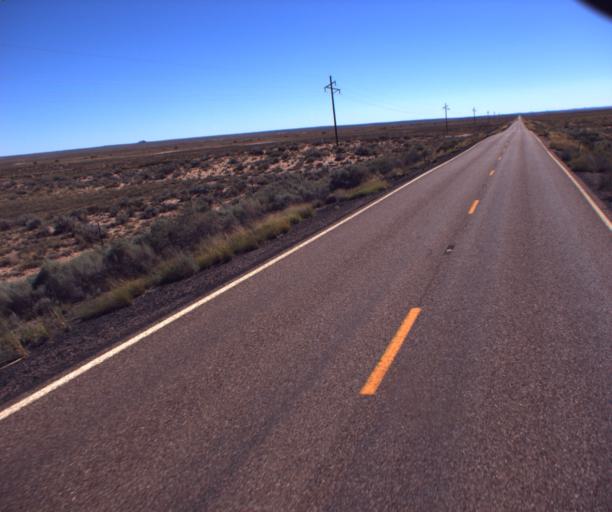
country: US
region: Arizona
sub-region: Navajo County
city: Holbrook
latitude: 35.1367
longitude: -110.0903
